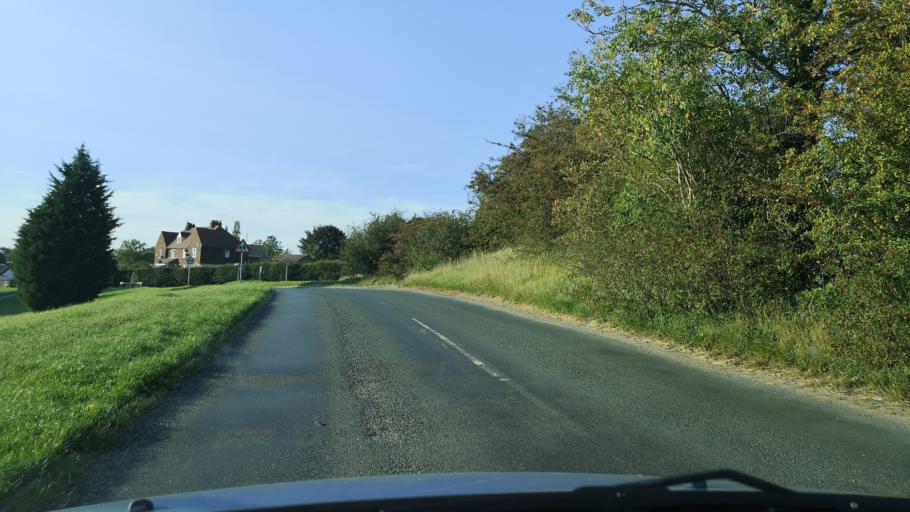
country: GB
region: England
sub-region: Doncaster
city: Norton
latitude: 53.6431
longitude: -1.2022
